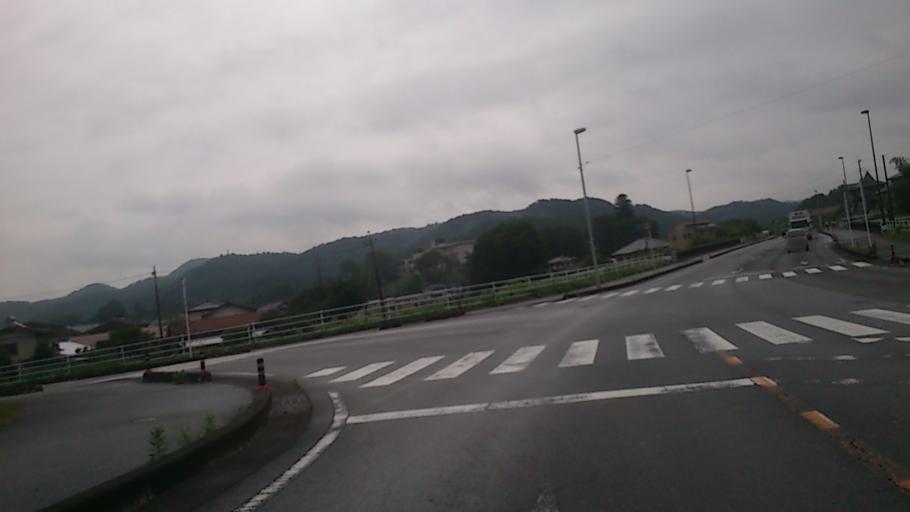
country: JP
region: Tochigi
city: Karasuyama
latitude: 36.7345
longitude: 140.1679
